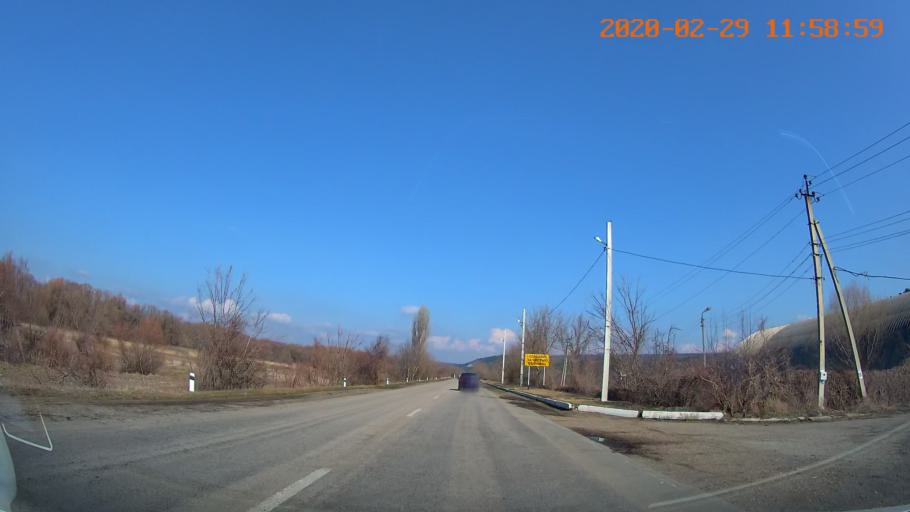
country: MD
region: Telenesti
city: Ribnita
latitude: 47.8198
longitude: 29.0142
